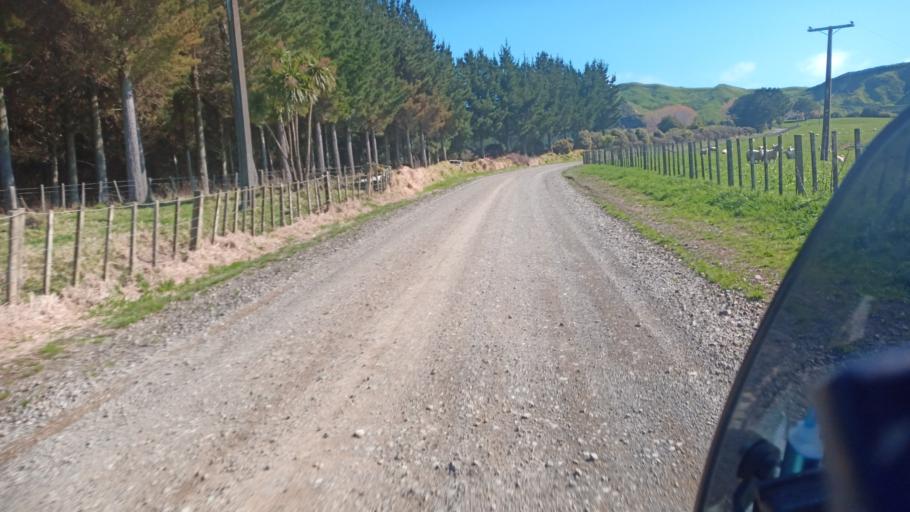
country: NZ
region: Gisborne
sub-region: Gisborne District
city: Gisborne
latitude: -39.1540
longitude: 177.9171
